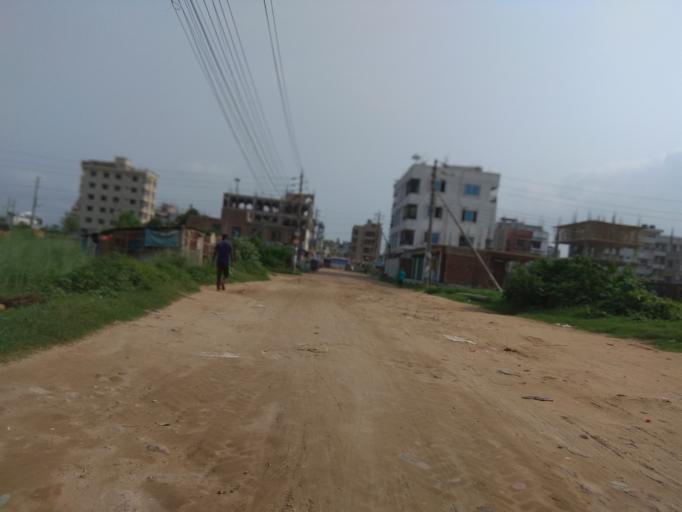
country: BD
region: Dhaka
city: Tungi
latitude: 23.8304
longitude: 90.3533
